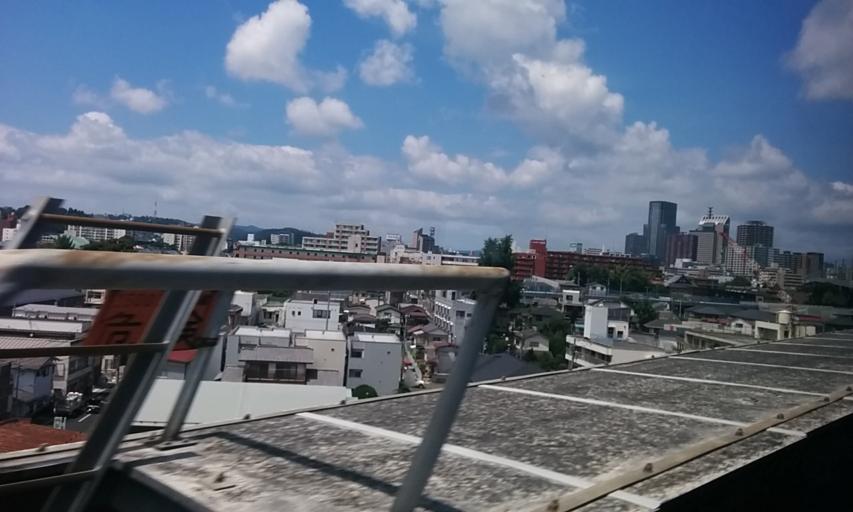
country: JP
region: Miyagi
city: Sendai
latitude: 38.2472
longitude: 140.8918
